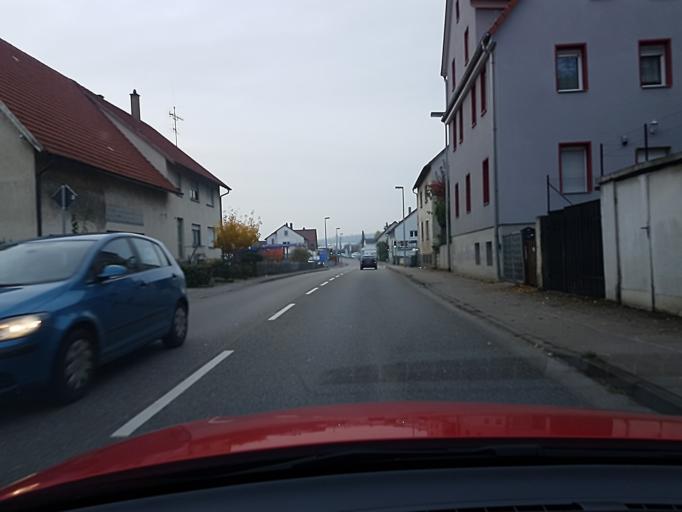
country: DE
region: Baden-Wuerttemberg
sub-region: Regierungsbezirk Stuttgart
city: Kirchheim am Neckar
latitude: 49.0410
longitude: 9.1441
